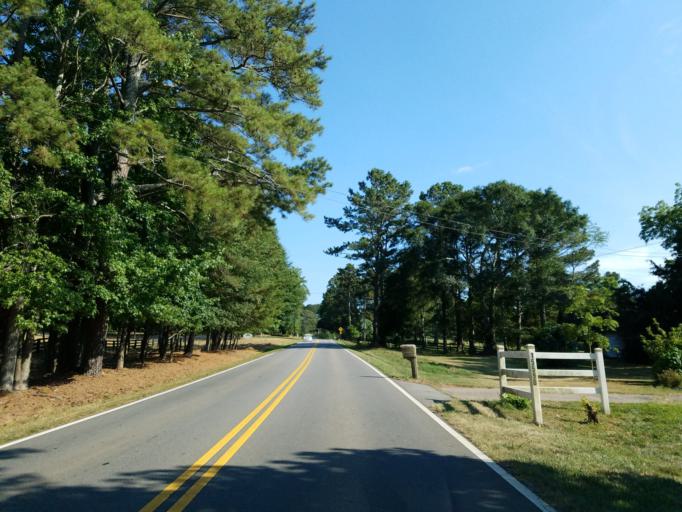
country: US
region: Georgia
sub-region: Fulton County
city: Milton
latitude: 34.1610
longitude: -84.3336
